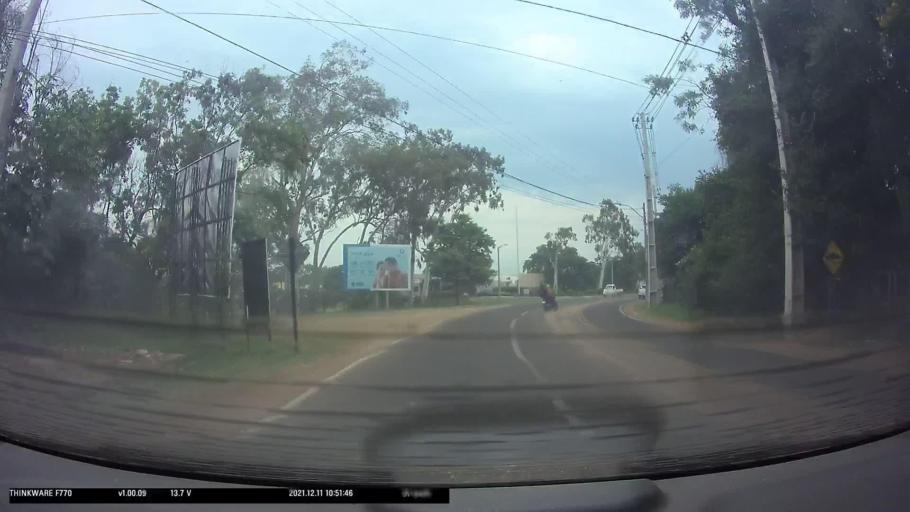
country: PY
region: Cordillera
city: San Bernardino
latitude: -25.2966
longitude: -57.2691
